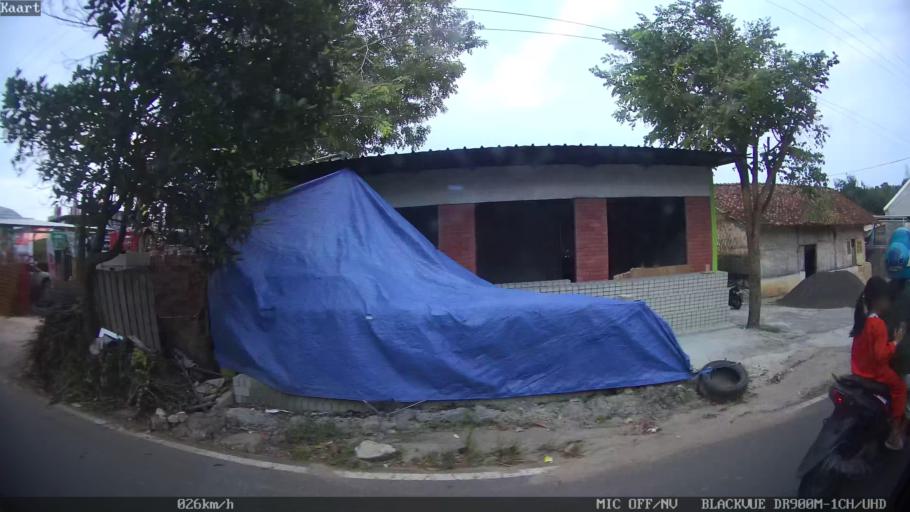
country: ID
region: Lampung
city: Bandarlampung
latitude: -5.4053
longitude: 105.2160
